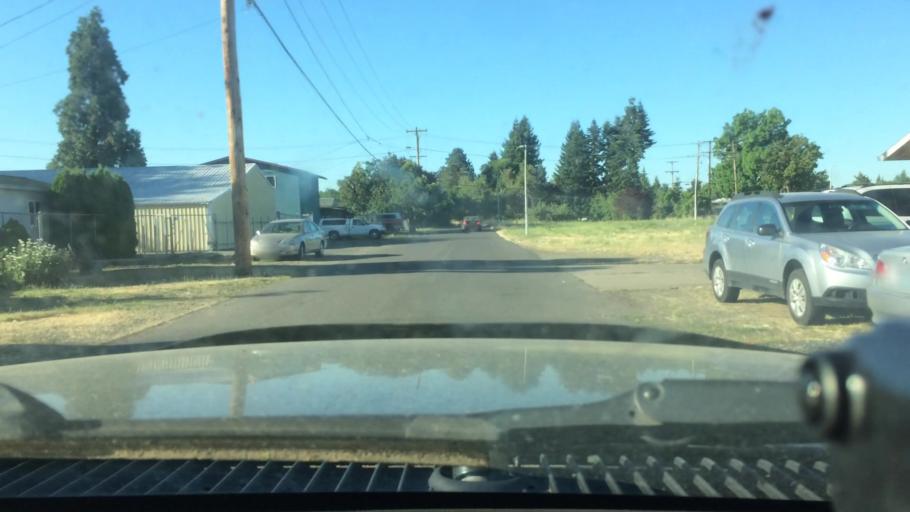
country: US
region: Oregon
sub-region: Lane County
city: Eugene
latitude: 44.1009
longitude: -123.1198
